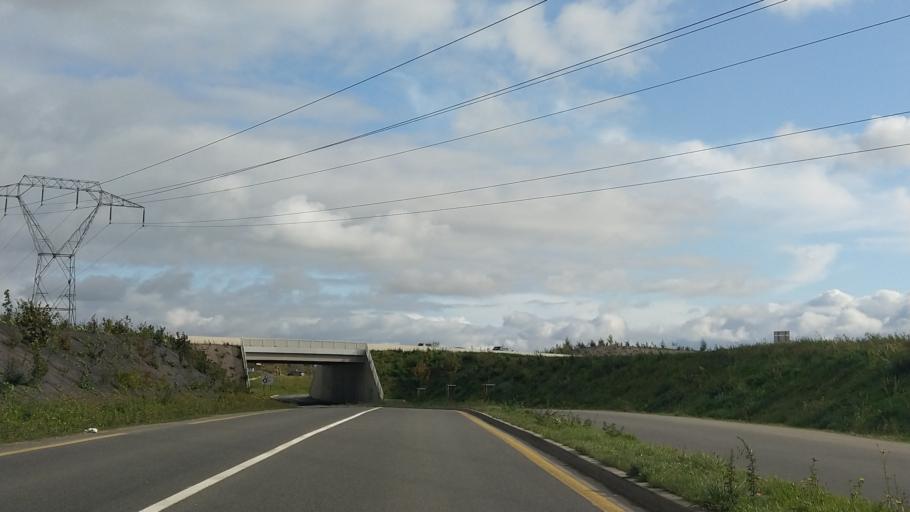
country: FR
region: Ile-de-France
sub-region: Departement du Val-d'Oise
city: Montsoult
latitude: 49.0608
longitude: 2.3291
